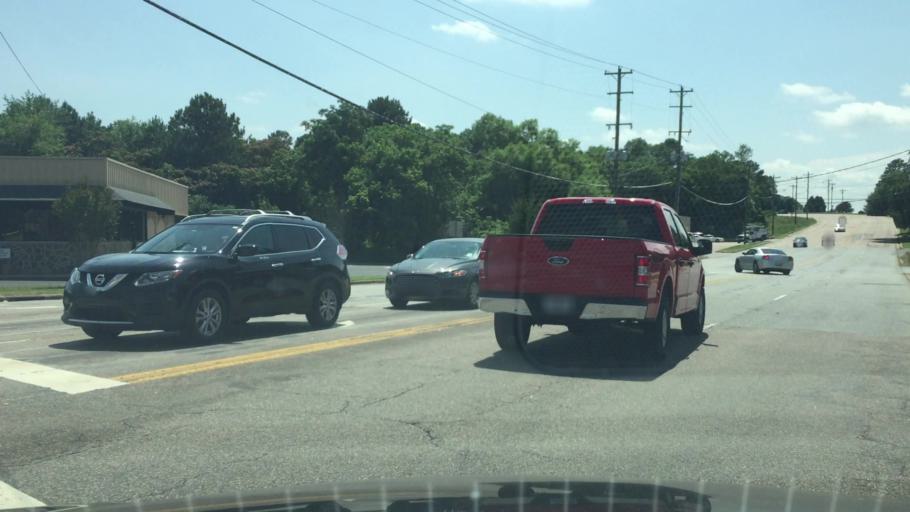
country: US
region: North Carolina
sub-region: Rowan County
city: Salisbury
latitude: 35.6645
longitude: -80.4995
